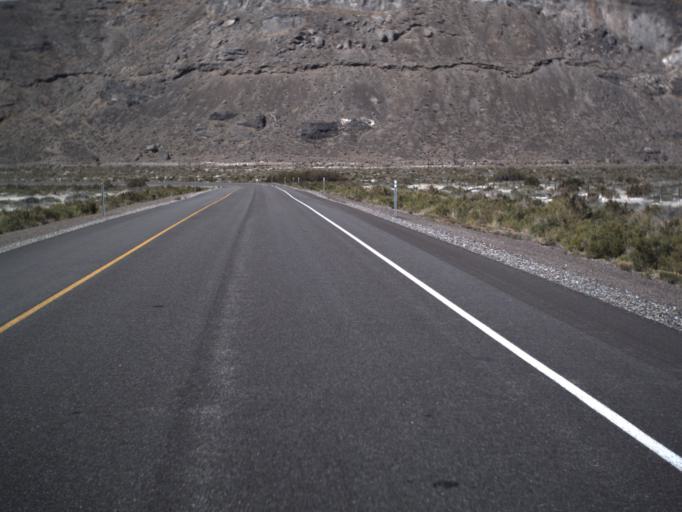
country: US
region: Utah
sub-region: Tooele County
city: Wendover
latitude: 40.7484
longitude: -114.0085
